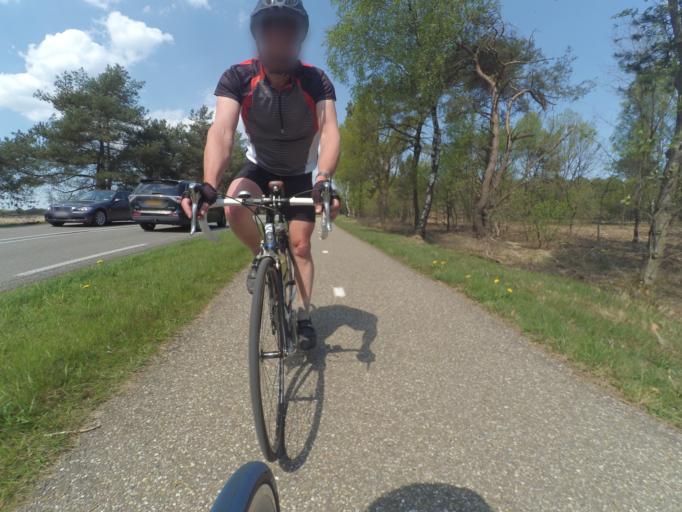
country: NL
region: Gelderland
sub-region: Gemeente Barneveld
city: Garderen
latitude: 52.2868
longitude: 5.6856
